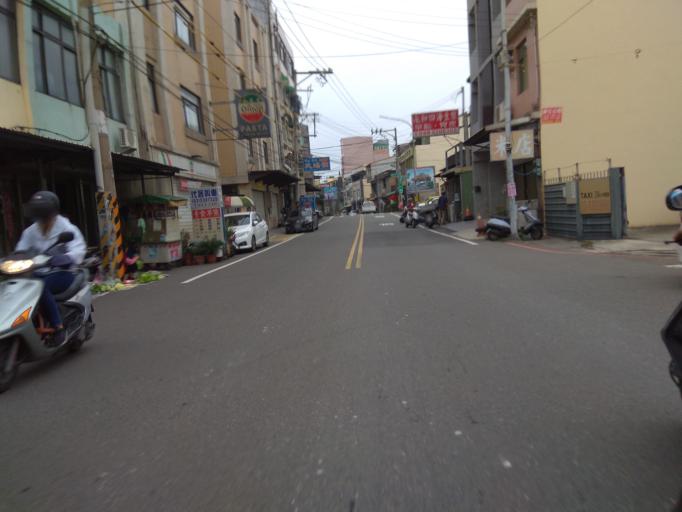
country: TW
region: Taiwan
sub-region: Hsinchu
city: Hsinchu
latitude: 24.7917
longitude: 120.9260
